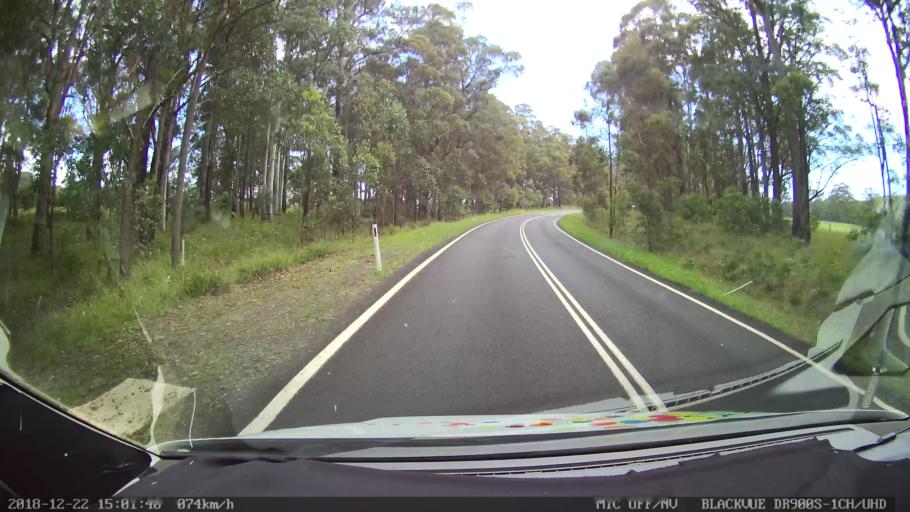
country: AU
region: New South Wales
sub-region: Bellingen
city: Dorrigo
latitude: -30.2570
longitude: 152.4576
